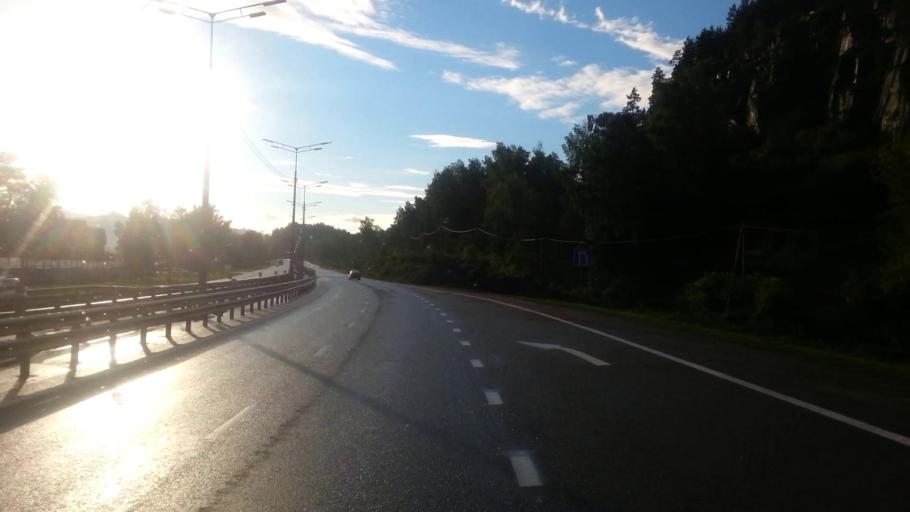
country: RU
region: Altay
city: Souzga
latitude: 51.9192
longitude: 85.8574
